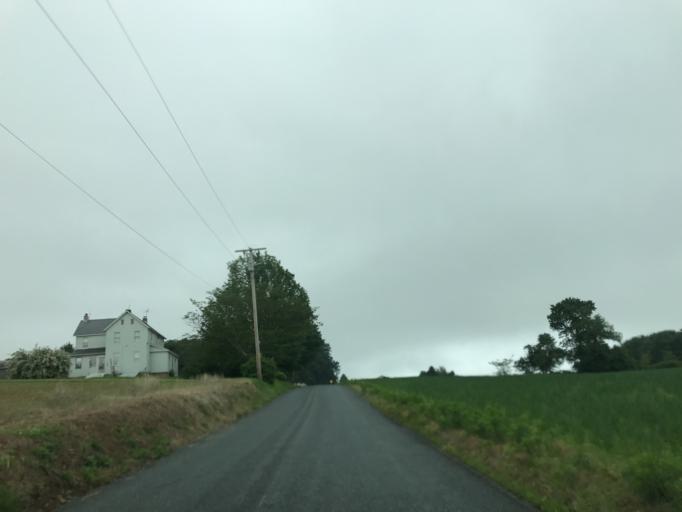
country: US
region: Pennsylvania
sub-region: York County
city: Stewartstown
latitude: 39.7062
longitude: -76.5107
